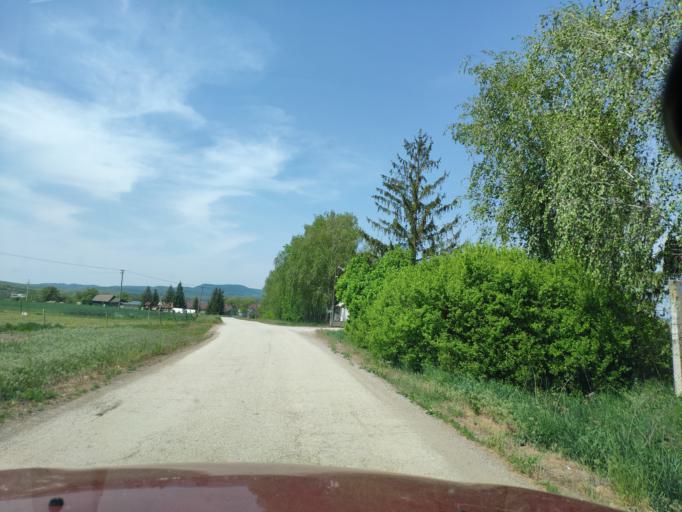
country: SK
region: Banskobystricky
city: Rimavska Sobota
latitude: 48.4154
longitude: 20.1502
